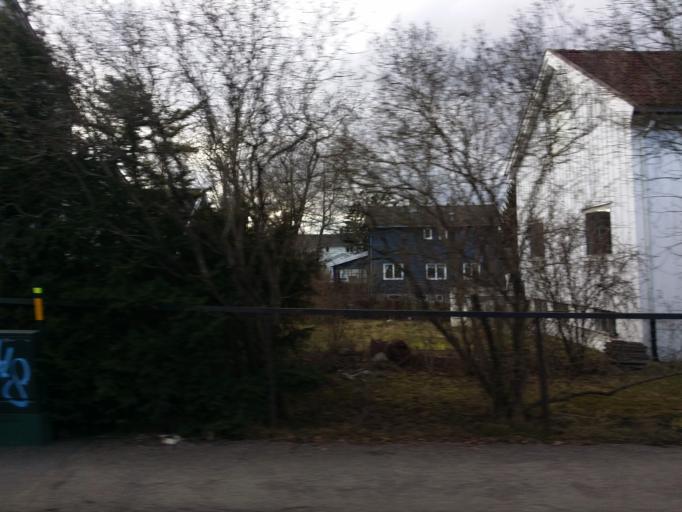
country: NO
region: Oslo
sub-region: Oslo
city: Oslo
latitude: 59.9577
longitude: 10.7856
